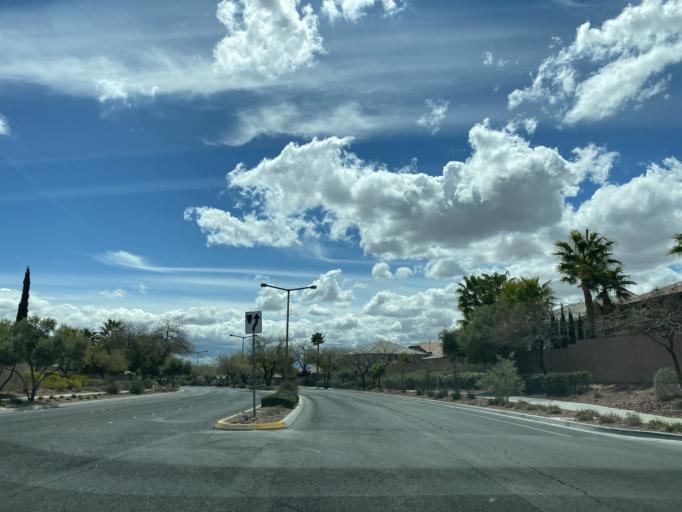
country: US
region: Nevada
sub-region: Clark County
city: Summerlin South
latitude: 36.1346
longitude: -115.3327
